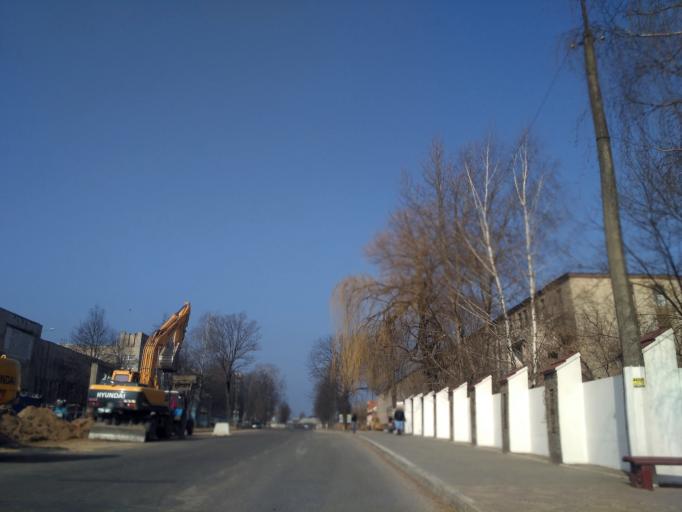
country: BY
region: Minsk
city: Horad Barysaw
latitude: 54.2280
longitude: 28.5194
